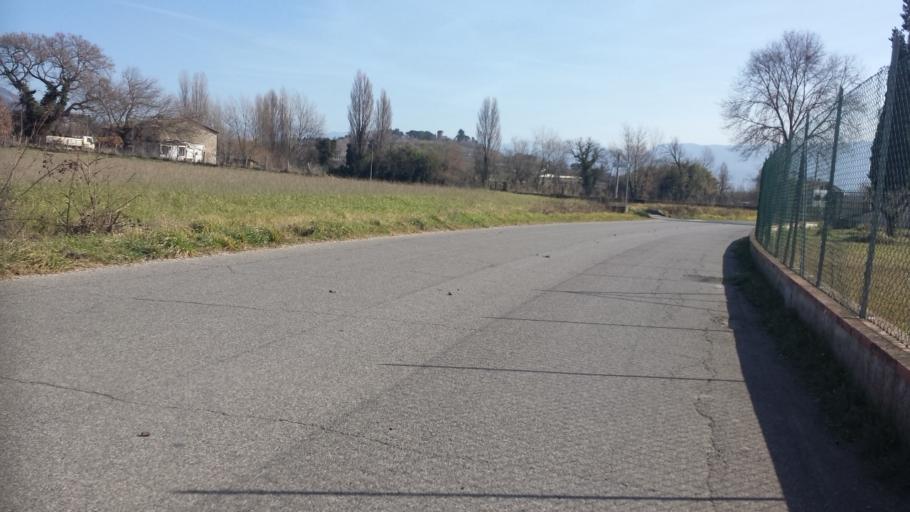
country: IT
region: Umbria
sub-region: Provincia di Terni
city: Terni
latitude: 42.5784
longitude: 12.5892
